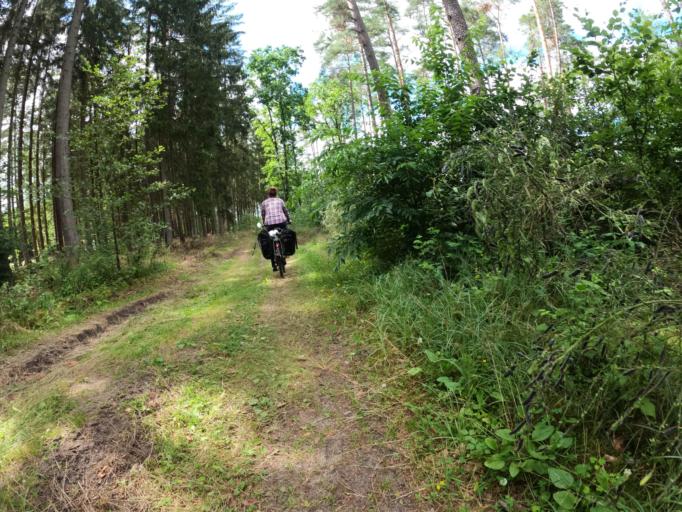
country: PL
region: West Pomeranian Voivodeship
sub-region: Powiat bialogardzki
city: Tychowo
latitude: 54.0067
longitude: 16.3601
